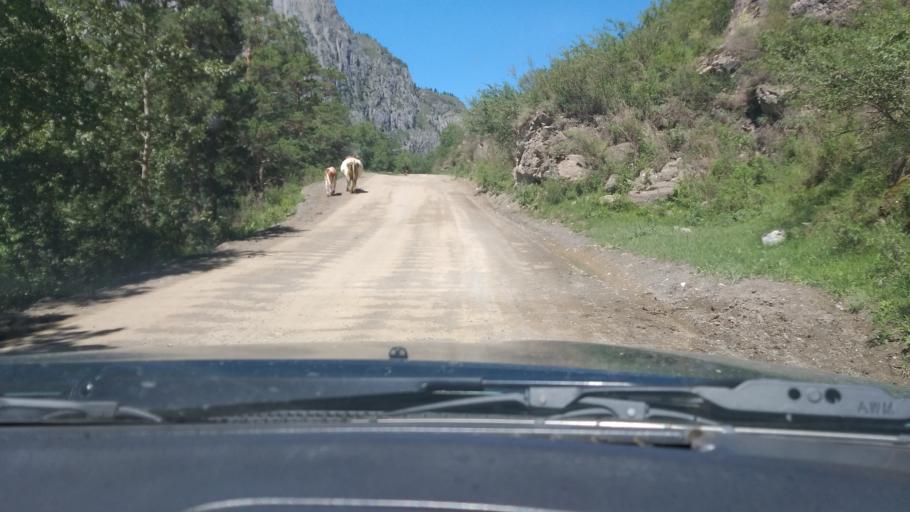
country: RU
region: Altay
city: Chemal
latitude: 51.2023
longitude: 86.0855
